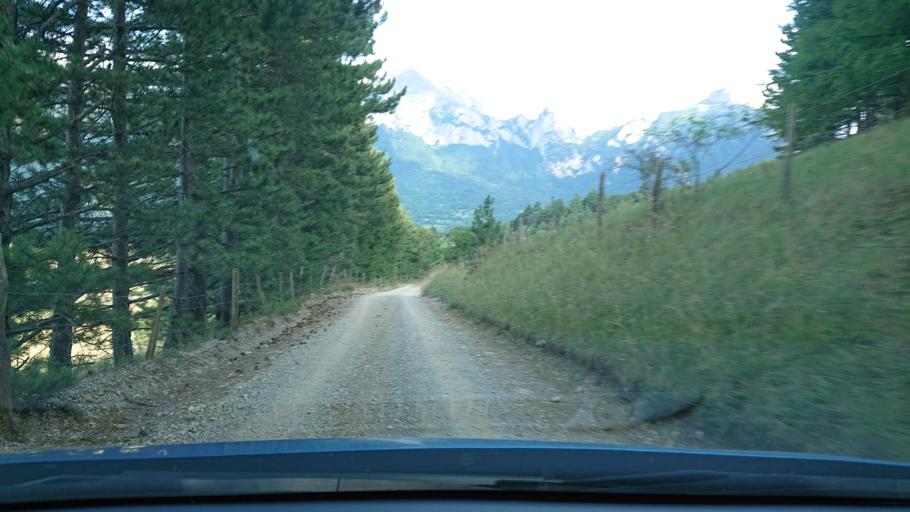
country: FR
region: Rhone-Alpes
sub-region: Departement de l'Isere
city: Mens
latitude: 44.7975
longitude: 5.8957
